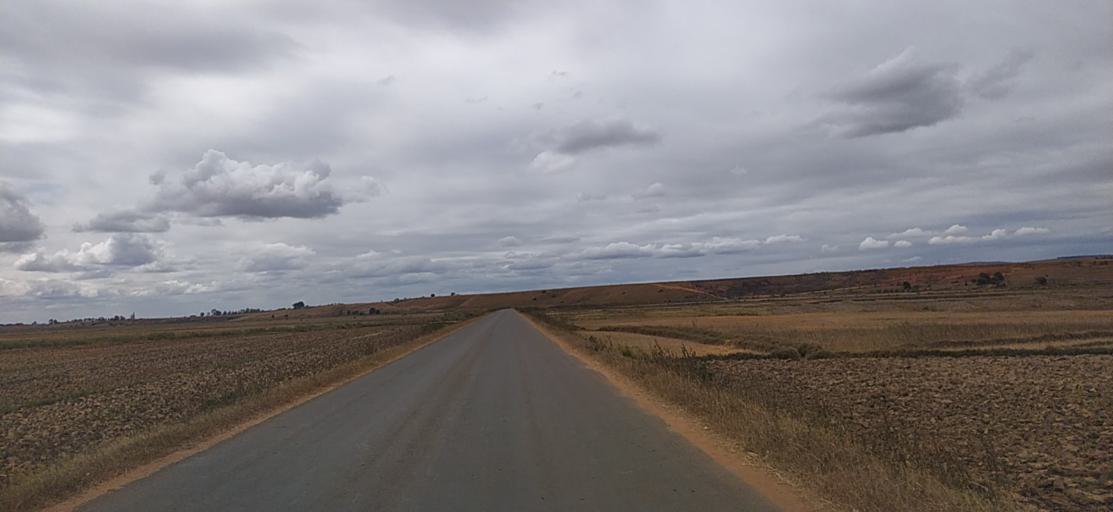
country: MG
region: Alaotra Mangoro
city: Ambatondrazaka
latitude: -17.9192
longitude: 48.2579
